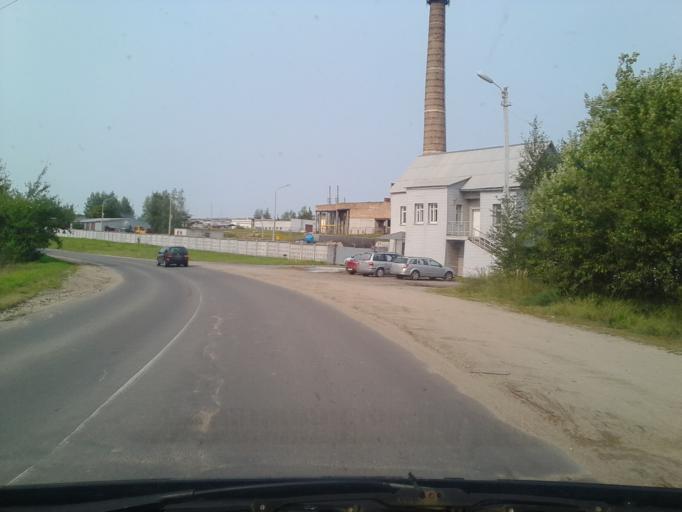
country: BY
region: Minsk
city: Hatava
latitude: 53.7714
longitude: 27.6511
